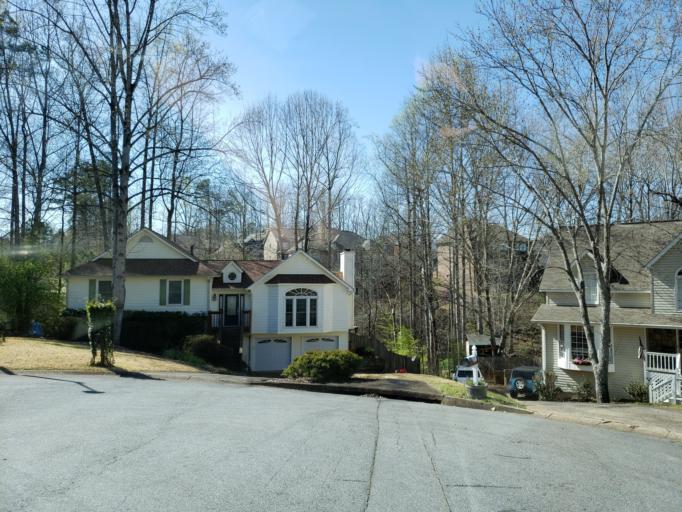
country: US
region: Georgia
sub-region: Cherokee County
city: Woodstock
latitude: 34.0363
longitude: -84.4936
